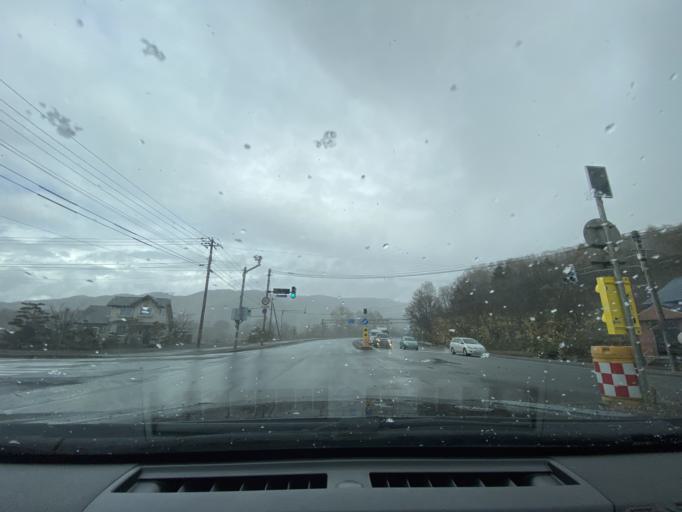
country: JP
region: Hokkaido
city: Fukagawa
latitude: 43.7274
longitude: 142.1873
